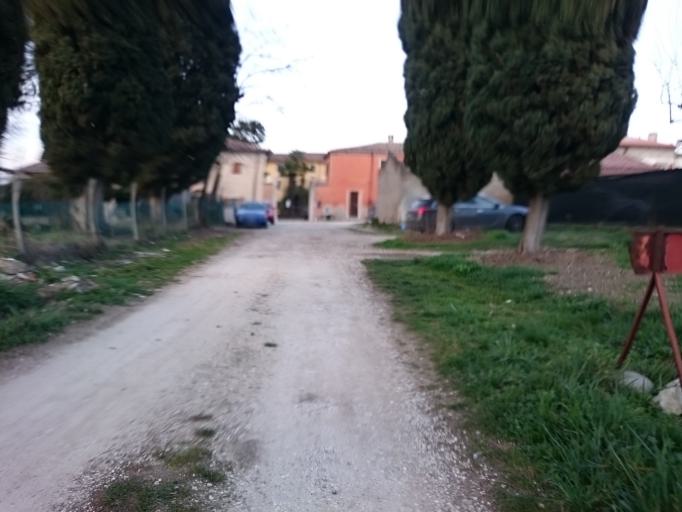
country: IT
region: Veneto
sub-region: Provincia di Verona
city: Cavalcaselle
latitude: 45.4545
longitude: 10.7100
